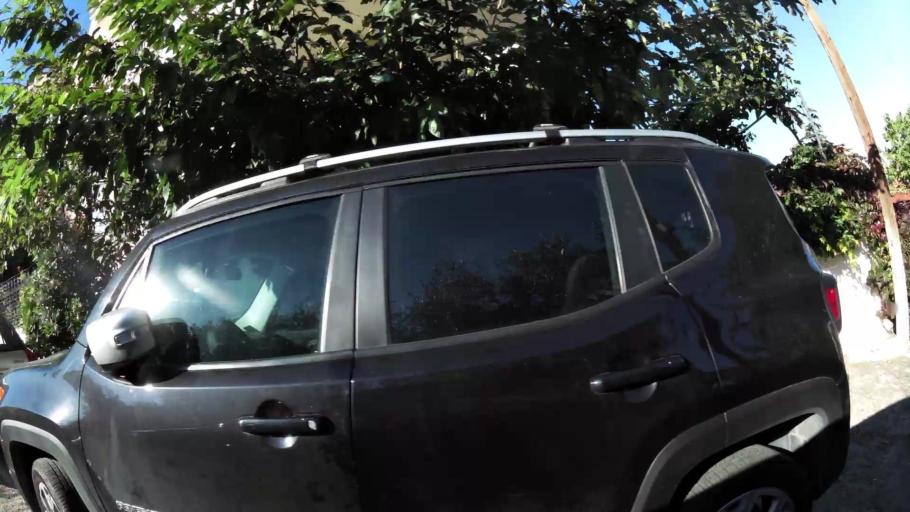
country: GR
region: Attica
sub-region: Nomarchia Anatolikis Attikis
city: Anoixi
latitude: 38.1376
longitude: 23.8645
